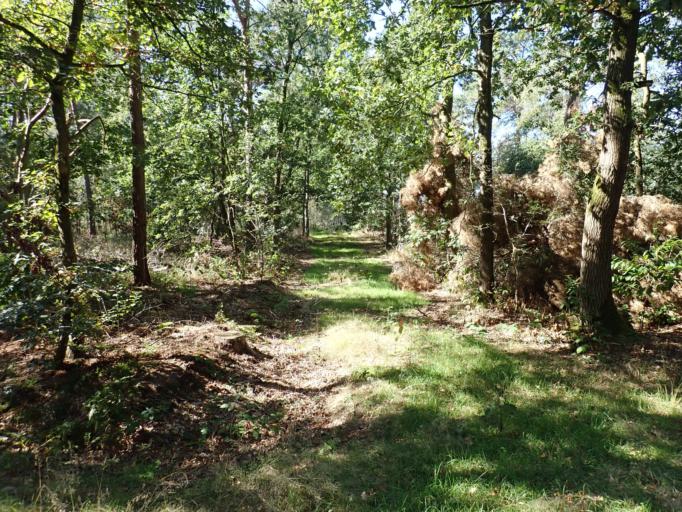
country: BE
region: Flanders
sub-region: Provincie Antwerpen
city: Baarle-Hertog
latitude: 51.4028
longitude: 4.8568
